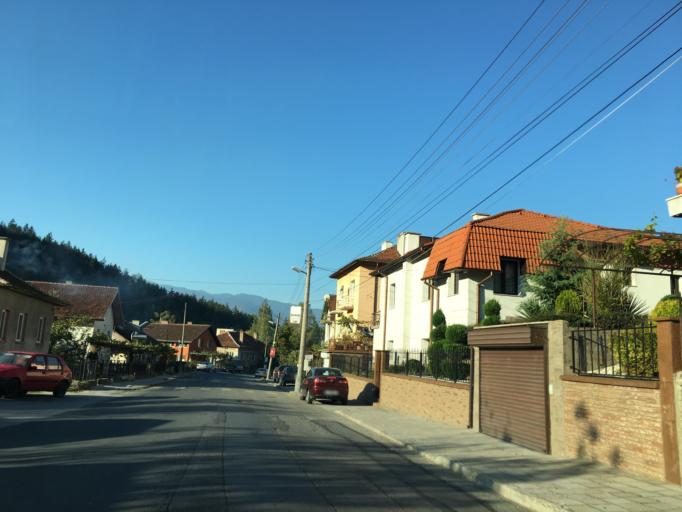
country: BG
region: Sofiya
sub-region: Obshtina Dolna Banya
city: Dolna Banya
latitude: 42.3344
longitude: 23.8768
